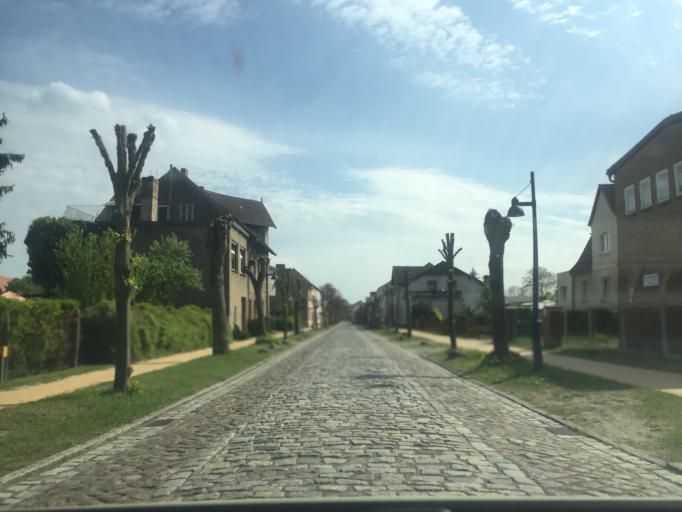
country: DE
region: Mecklenburg-Vorpommern
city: Torgelow
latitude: 53.6327
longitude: 14.0068
